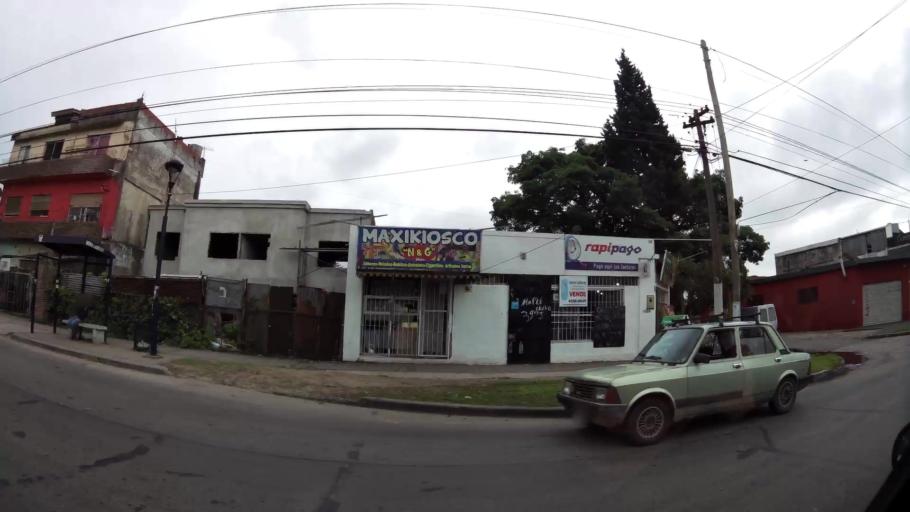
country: AR
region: Buenos Aires
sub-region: Partido de Quilmes
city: Quilmes
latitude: -34.7812
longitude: -58.2462
